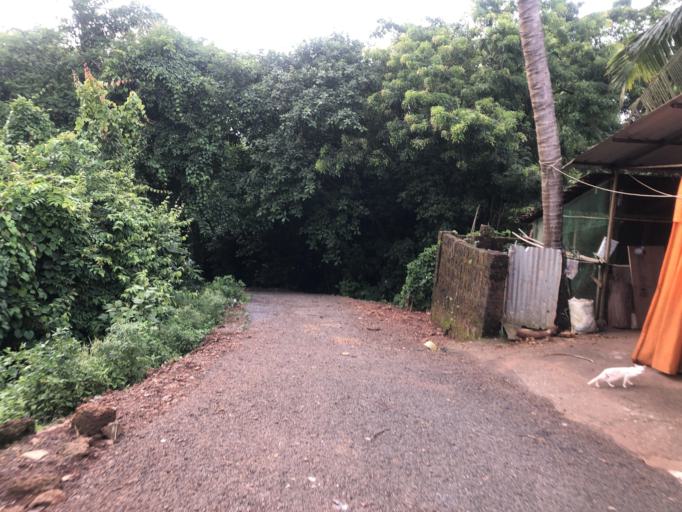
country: IN
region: Goa
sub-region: North Goa
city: Serula
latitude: 15.5495
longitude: 73.8247
